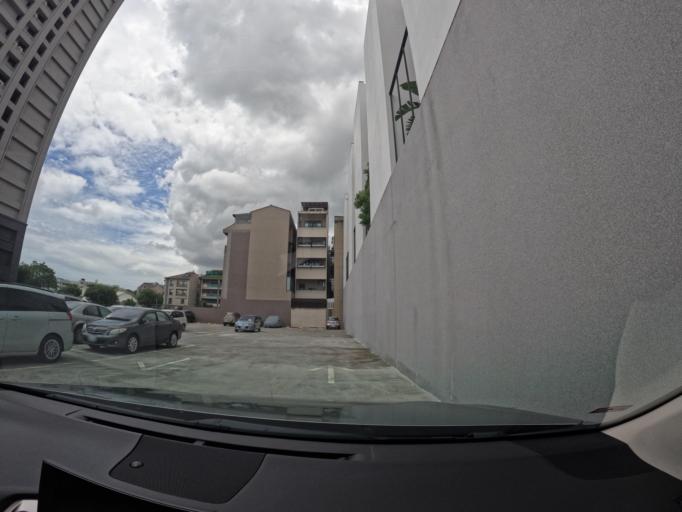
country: TW
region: Kaohsiung
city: Kaohsiung
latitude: 22.7269
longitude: 120.2955
